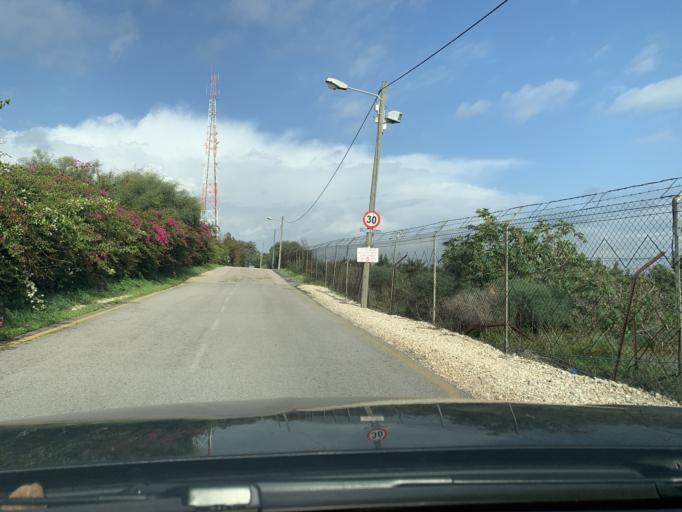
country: PS
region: West Bank
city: Qalqilyah
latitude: 32.1942
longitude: 34.9522
